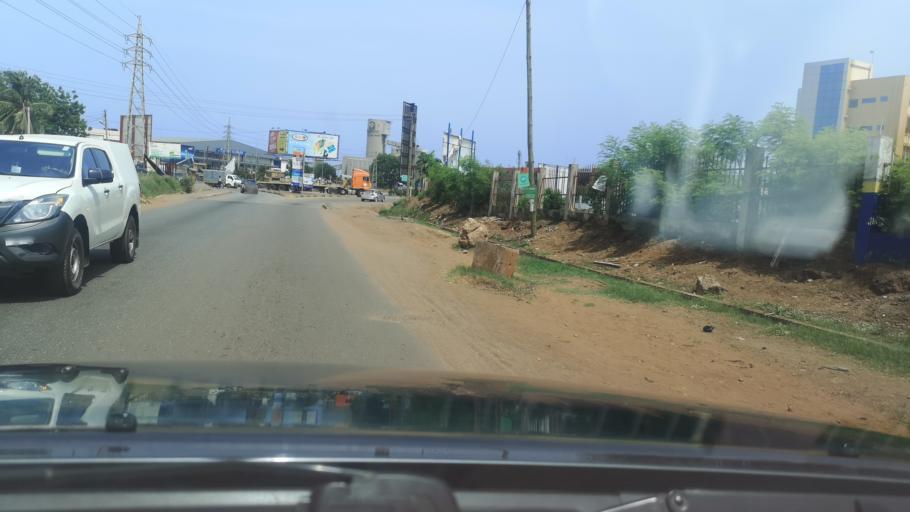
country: GH
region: Greater Accra
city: Tema
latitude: 5.6388
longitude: 0.0027
